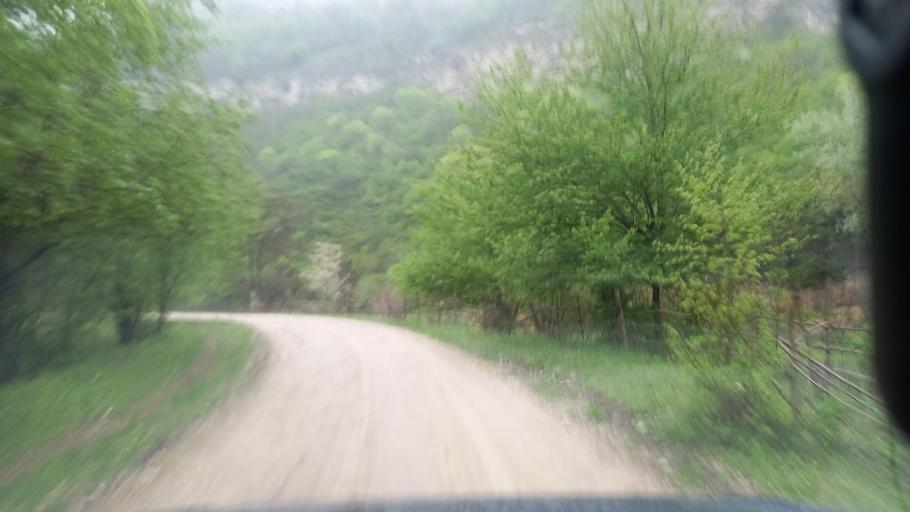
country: RU
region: Kabardino-Balkariya
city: Gundelen
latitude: 43.5911
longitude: 43.1253
